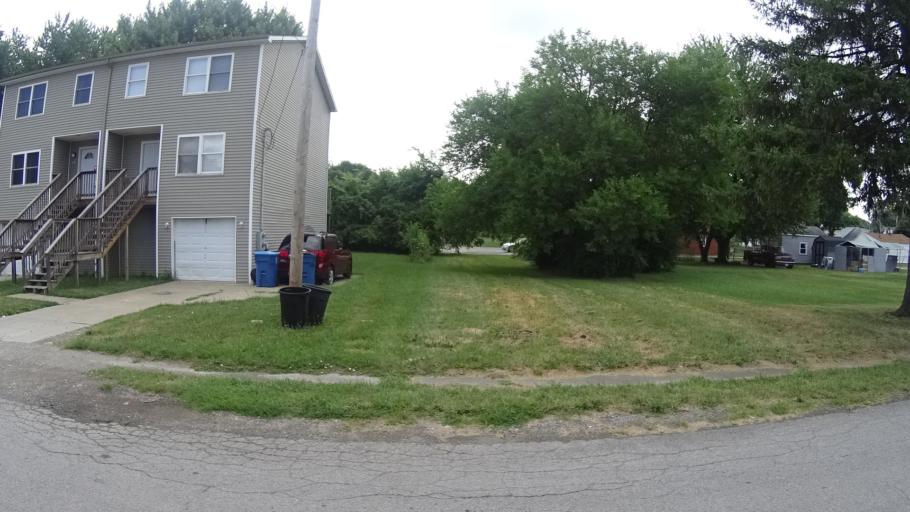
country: US
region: Ohio
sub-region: Erie County
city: Sandusky
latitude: 41.4397
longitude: -82.7248
